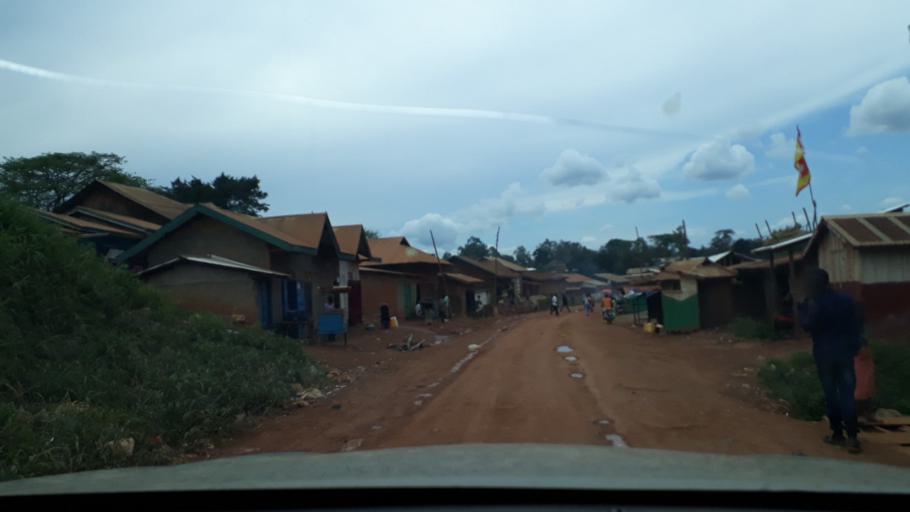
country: CD
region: Eastern Province
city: Bunia
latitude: 1.7388
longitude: 30.3411
